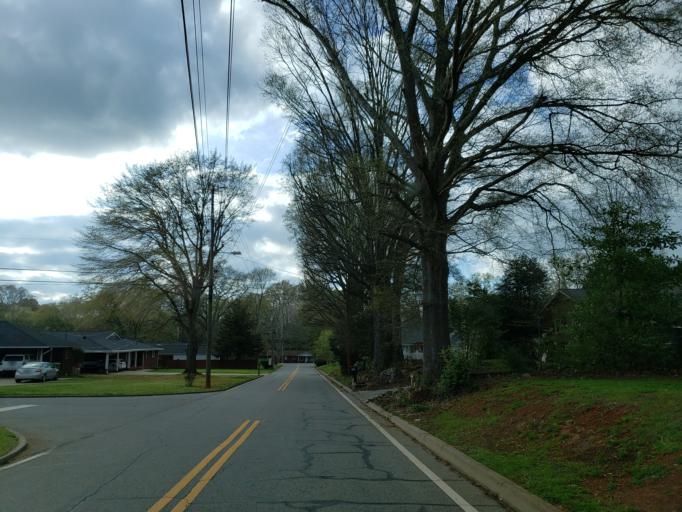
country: US
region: Georgia
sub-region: Bartow County
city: Cartersville
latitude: 34.1578
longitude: -84.8028
